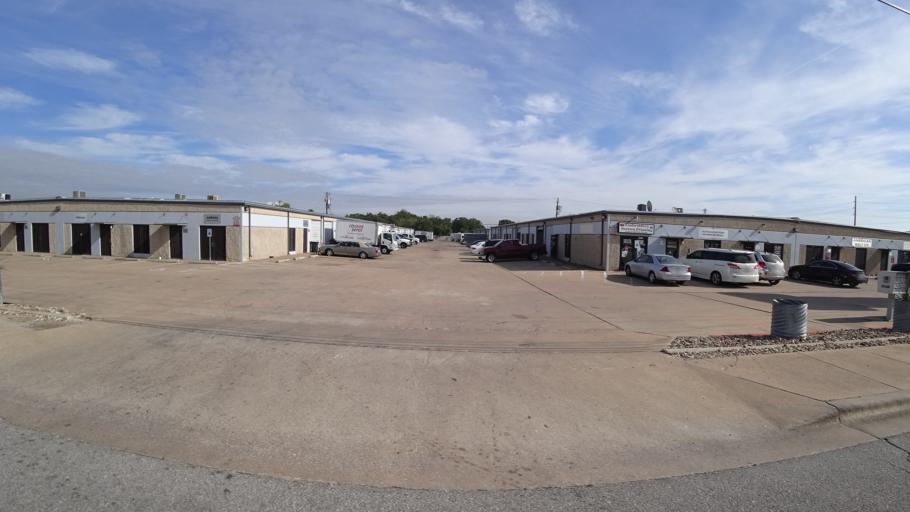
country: US
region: Texas
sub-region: Travis County
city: Austin
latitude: 30.2103
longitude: -97.7263
